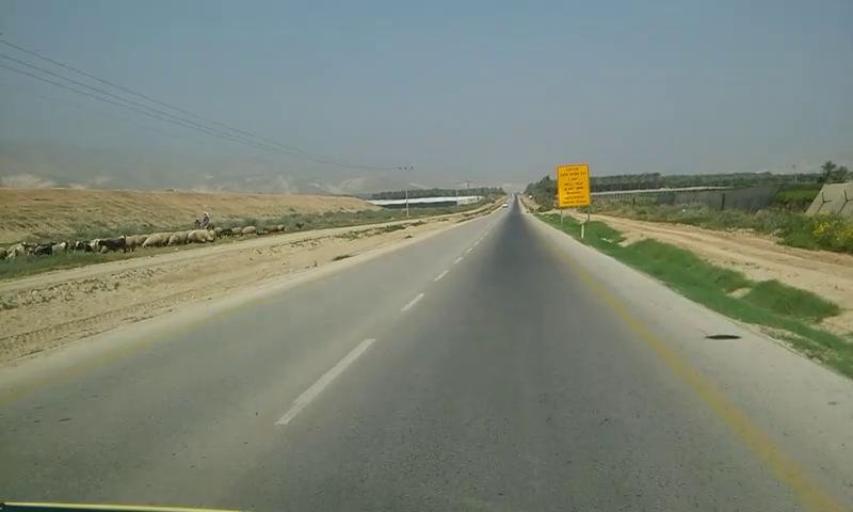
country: PS
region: West Bank
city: Al `Awja
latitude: 31.9888
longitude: 35.4607
